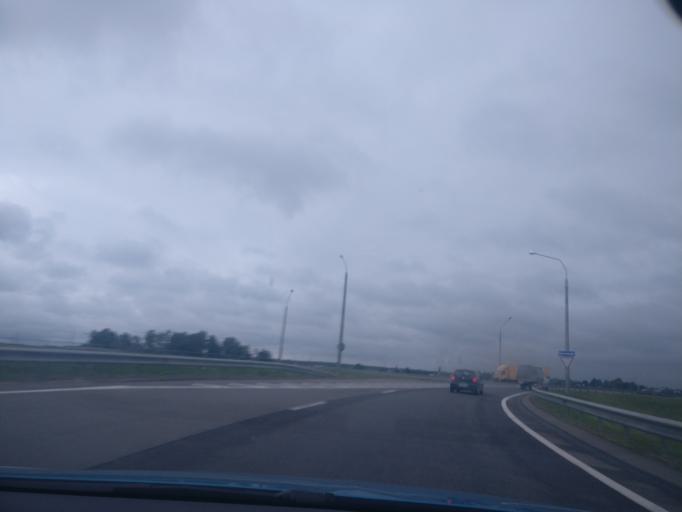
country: BY
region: Minsk
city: Slabada
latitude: 54.0167
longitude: 27.8929
